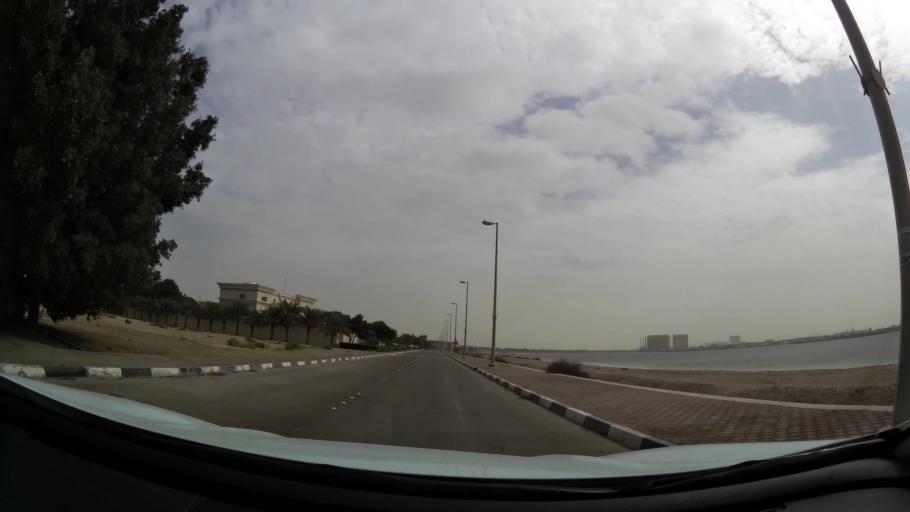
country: AE
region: Abu Dhabi
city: Abu Dhabi
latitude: 24.3923
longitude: 54.5054
